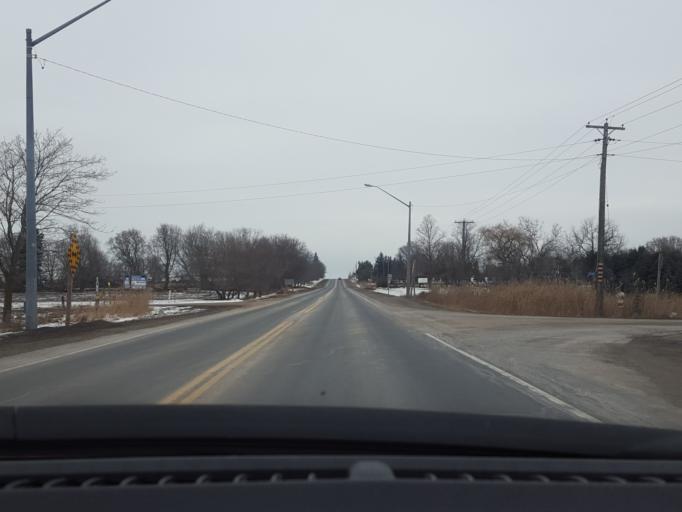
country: CA
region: Ontario
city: Newmarket
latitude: 44.1253
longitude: -79.4212
